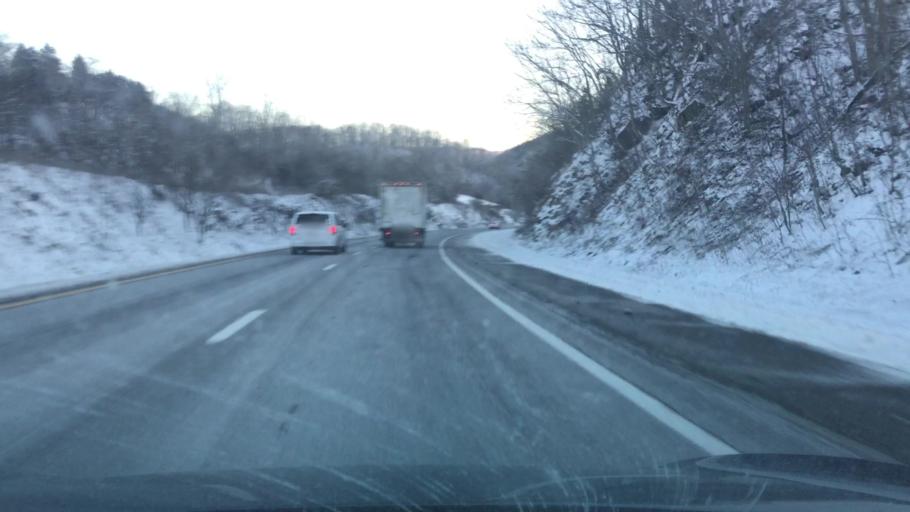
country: US
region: Virginia
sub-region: Montgomery County
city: Shawsville
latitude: 37.2043
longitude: -80.2658
